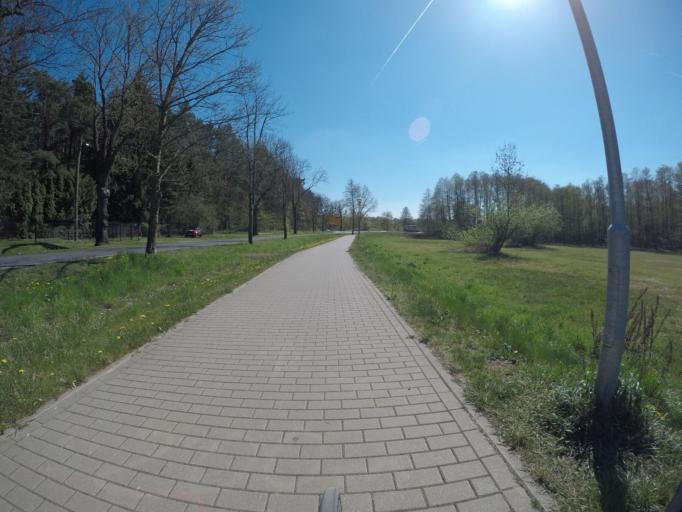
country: DE
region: Brandenburg
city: Strausberg
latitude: 52.5947
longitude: 13.8916
